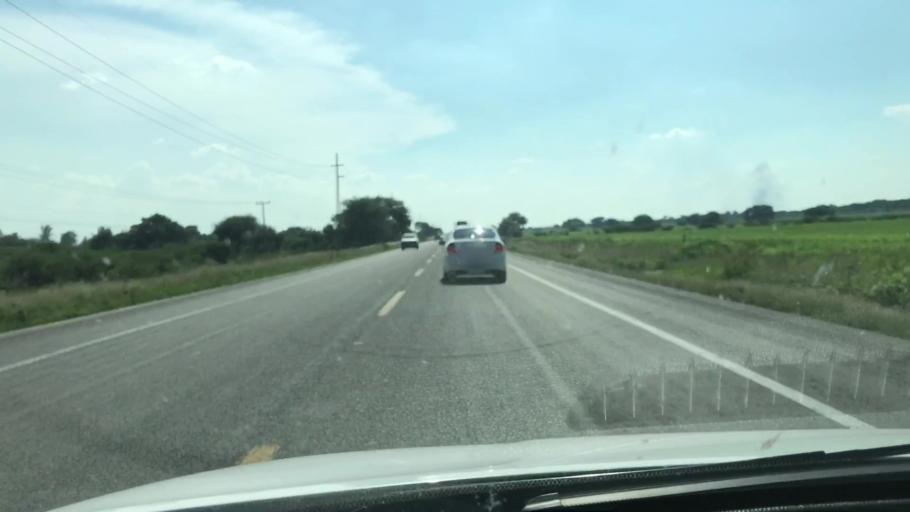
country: MX
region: Michoacan
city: Vistahermosa de Negrete
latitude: 20.2726
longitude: -102.4184
